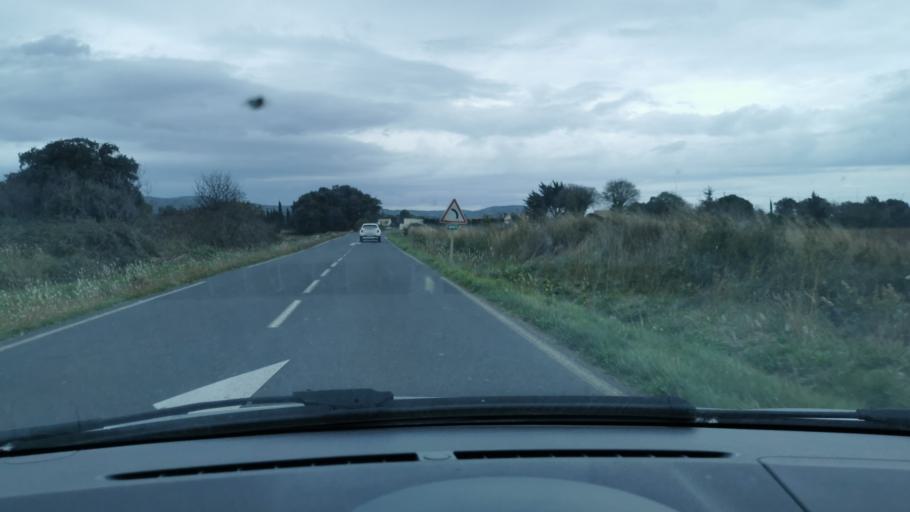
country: FR
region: Languedoc-Roussillon
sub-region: Departement de l'Herault
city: Balaruc-le-Vieux
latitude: 43.4404
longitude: 3.7127
